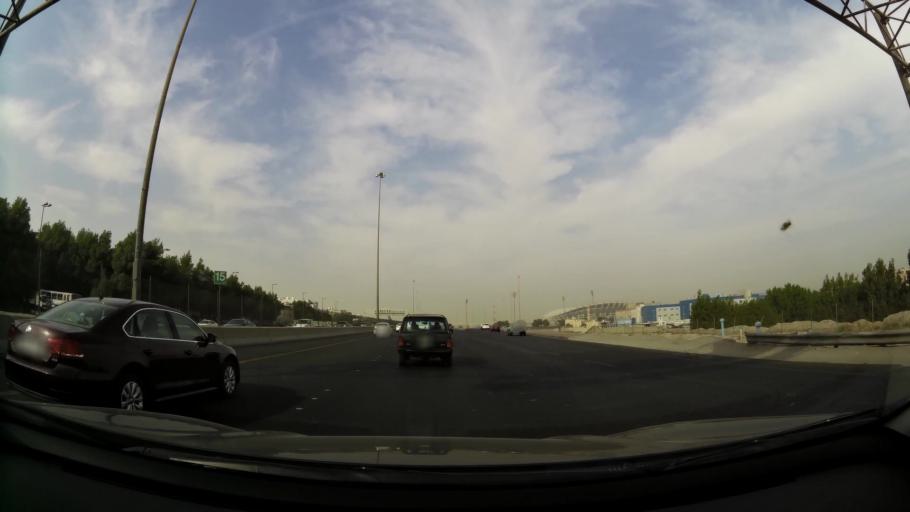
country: KW
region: Al Asimah
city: Ar Rabiyah
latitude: 29.2671
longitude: 47.9310
